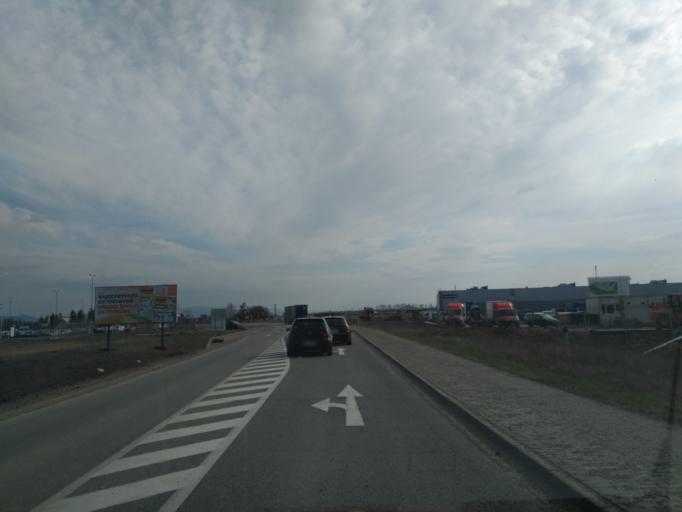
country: SK
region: Kosicky
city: Kosice
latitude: 48.6783
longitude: 21.2305
